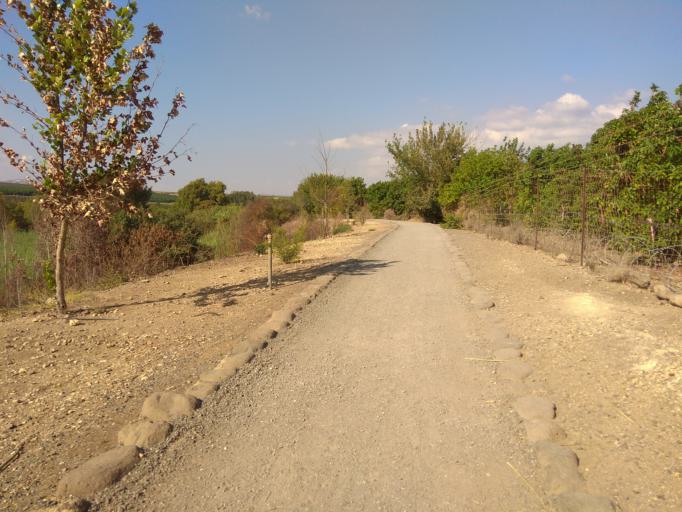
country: IL
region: Northern District
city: Qiryat Shemona
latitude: 33.2282
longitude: 35.6188
